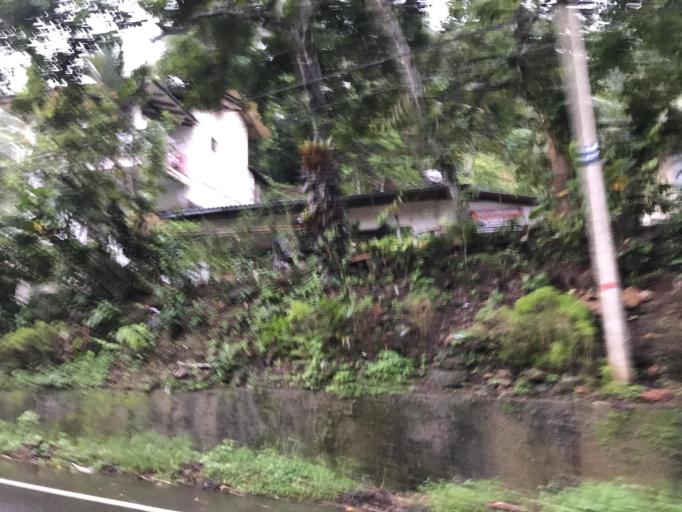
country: LK
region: Western
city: Horawala Junction
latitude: 6.5212
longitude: 80.2031
